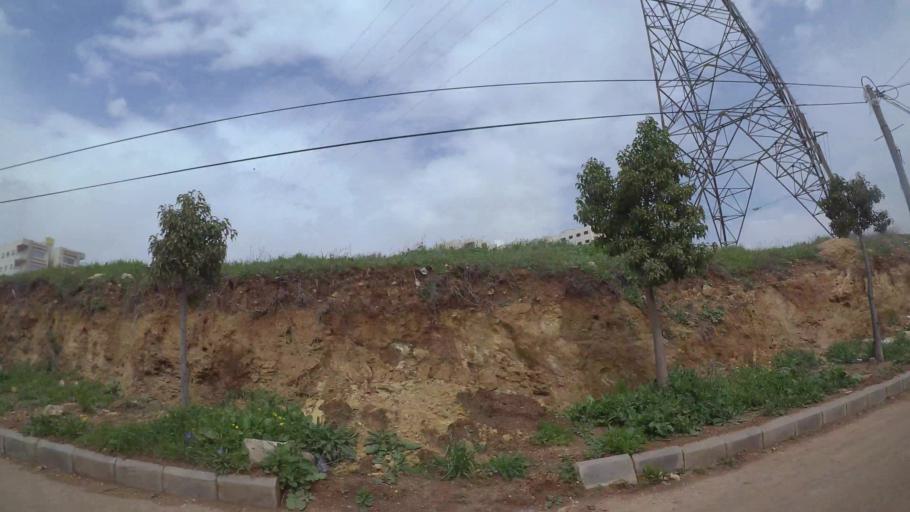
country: JO
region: Amman
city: Umm as Summaq
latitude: 31.9003
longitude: 35.8324
